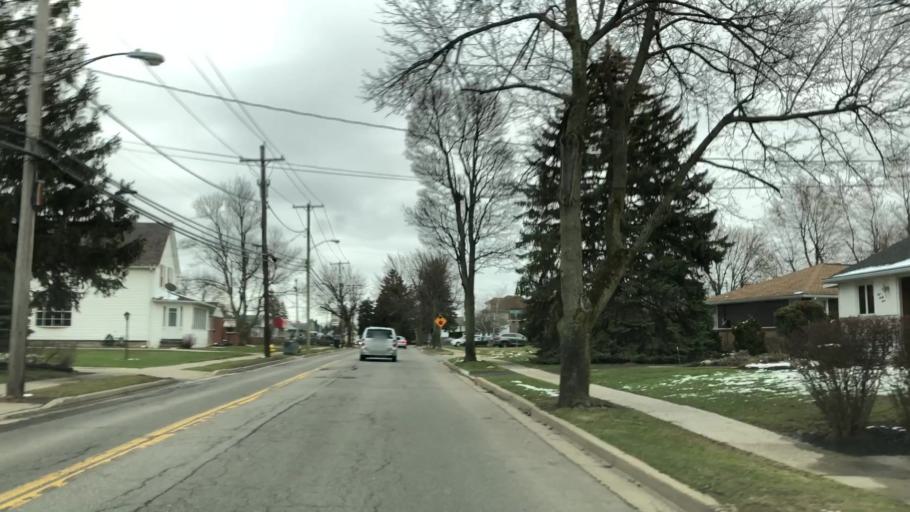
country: US
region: New York
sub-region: Erie County
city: Lancaster
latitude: 42.8942
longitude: -78.6759
